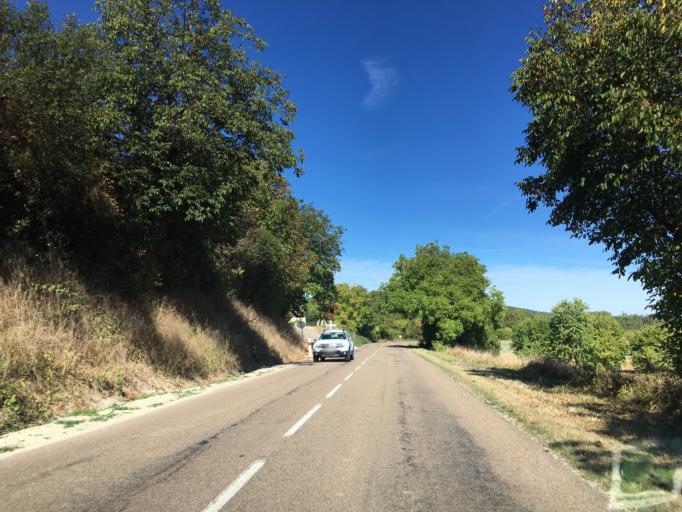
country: FR
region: Bourgogne
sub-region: Departement de l'Yonne
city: Vermenton
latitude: 47.6240
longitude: 3.6636
